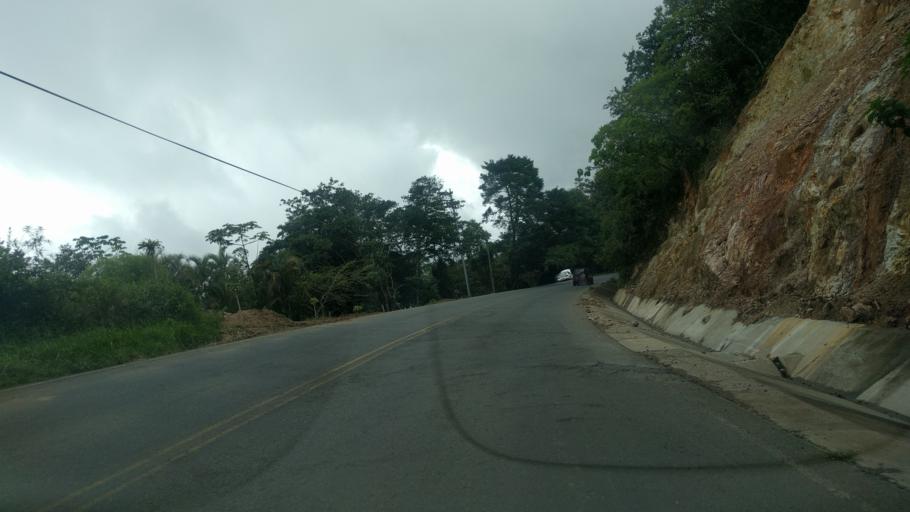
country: CR
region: Alajuela
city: San Rafael
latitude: 10.0332
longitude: -84.5115
